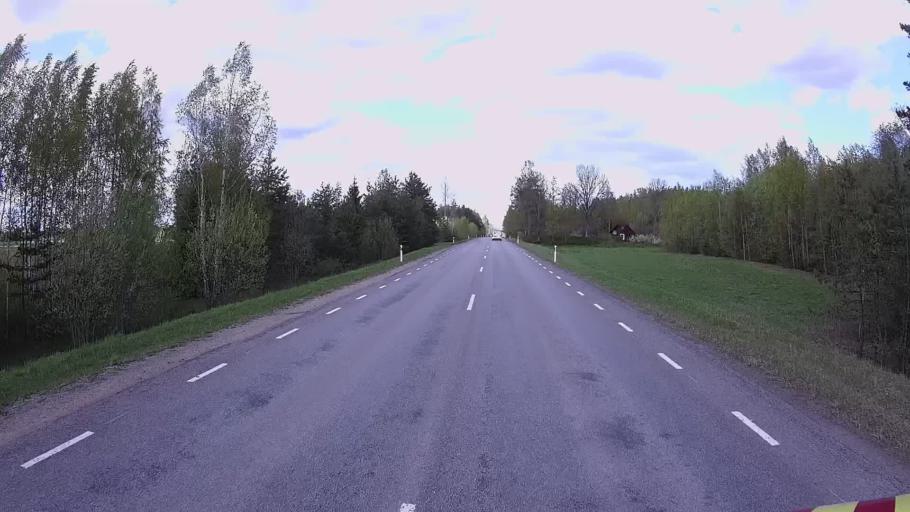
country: EE
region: Tartu
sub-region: Alatskivi vald
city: Kallaste
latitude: 58.5212
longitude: 27.0037
